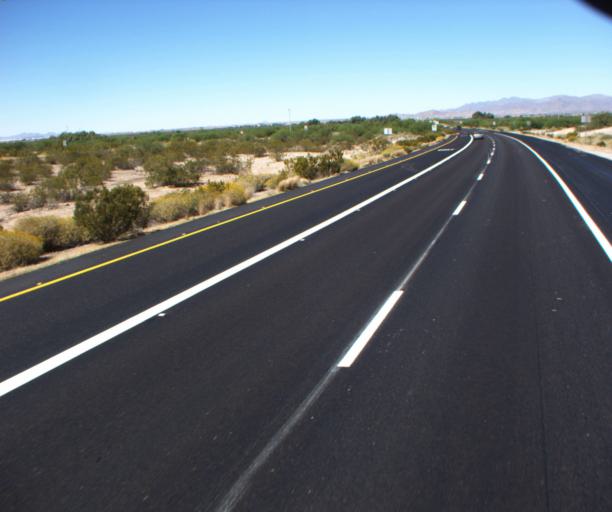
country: US
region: Arizona
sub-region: Maricopa County
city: Buckeye
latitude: 33.3167
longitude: -112.6231
